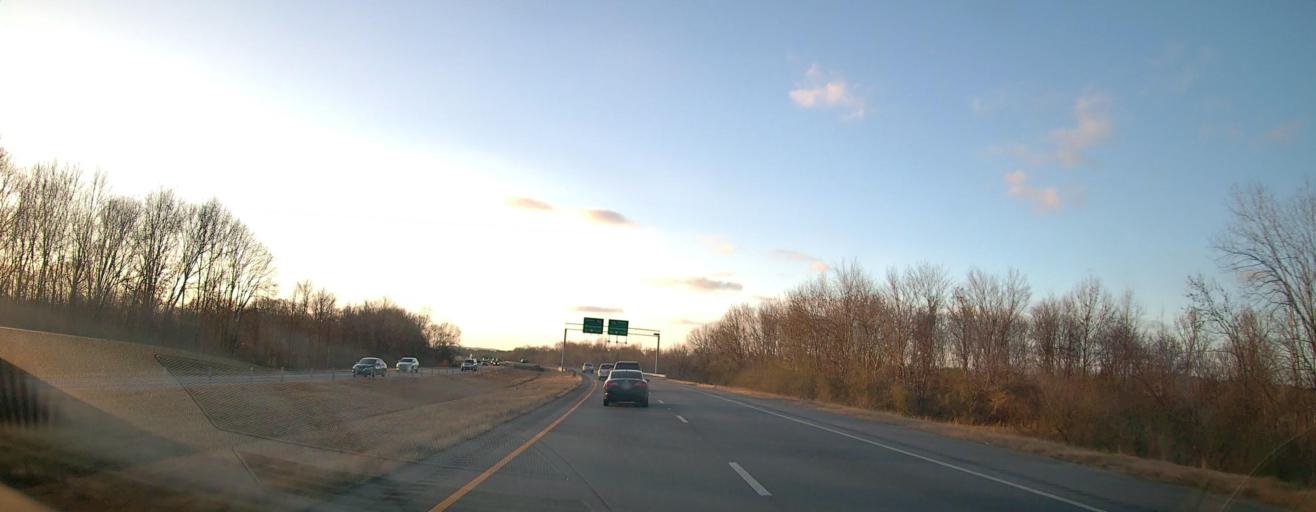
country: US
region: Alabama
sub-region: Etowah County
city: Attalla
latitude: 34.0029
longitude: -86.0626
